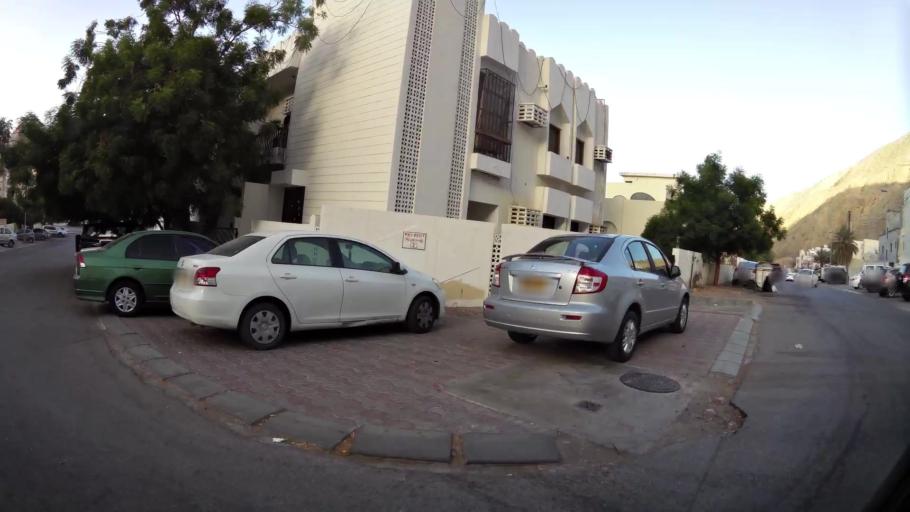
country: OM
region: Muhafazat Masqat
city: Muscat
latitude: 23.5688
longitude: 58.5687
